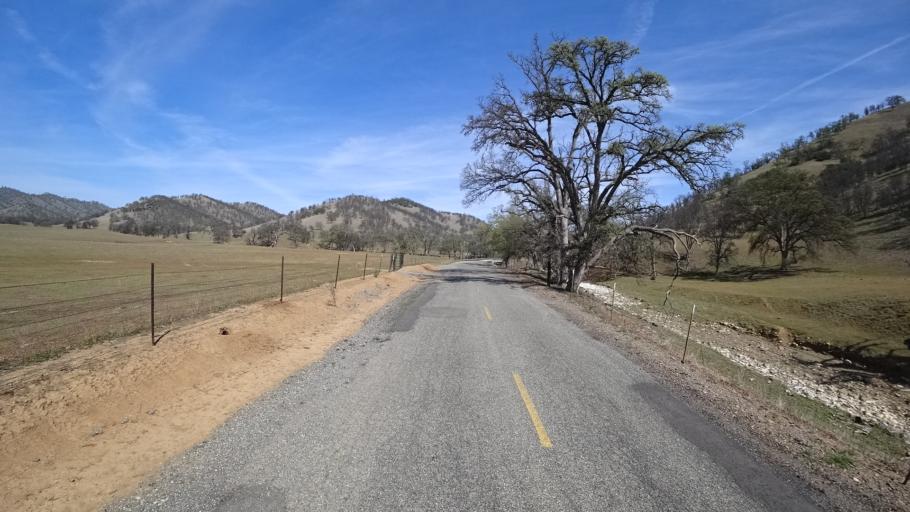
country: US
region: California
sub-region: Glenn County
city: Willows
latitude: 39.5279
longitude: -122.4576
